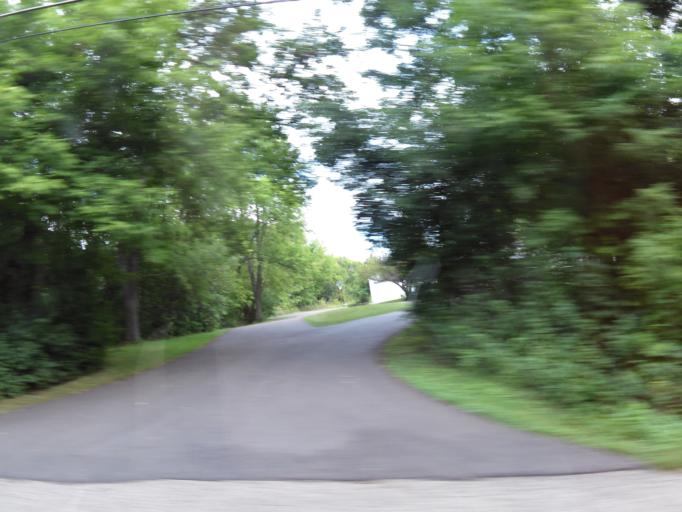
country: US
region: Minnesota
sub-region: Washington County
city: Bayport
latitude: 44.9812
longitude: -92.8223
